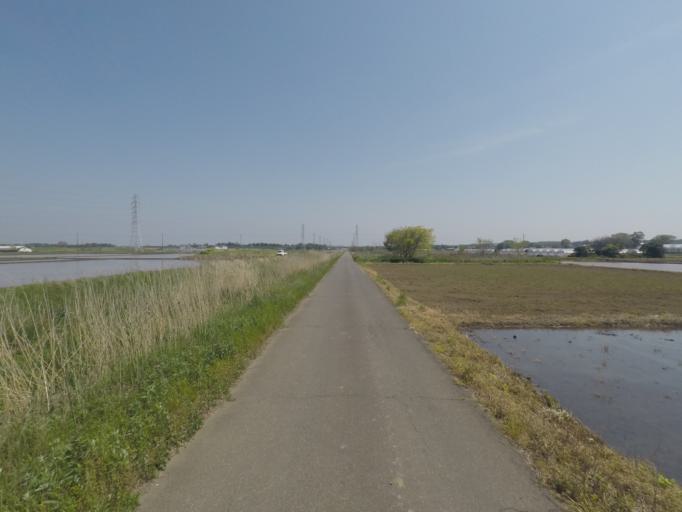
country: JP
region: Ibaraki
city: Naka
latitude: 36.1003
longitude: 140.1593
